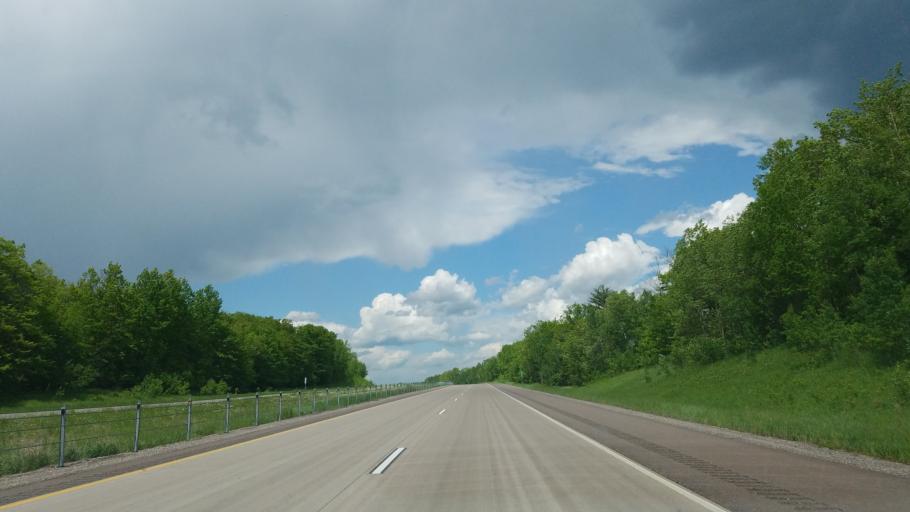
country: US
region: Minnesota
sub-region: Carlton County
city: Moose Lake
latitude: 46.4632
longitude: -92.7217
